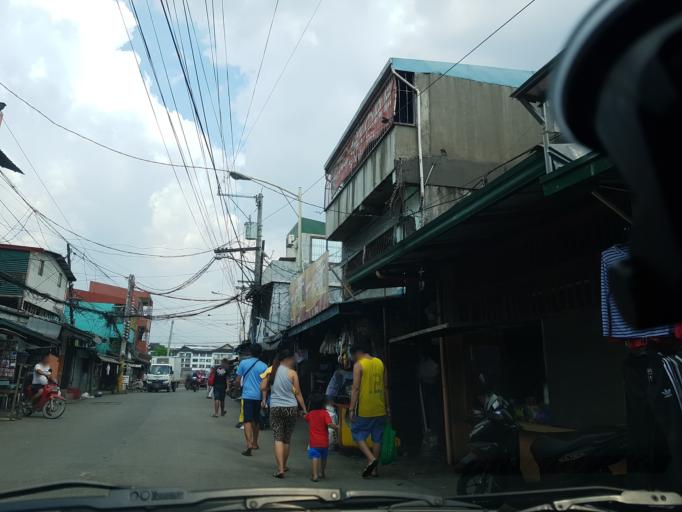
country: PH
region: Metro Manila
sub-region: Pasig
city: Pasig City
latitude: 14.5896
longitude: 121.0916
